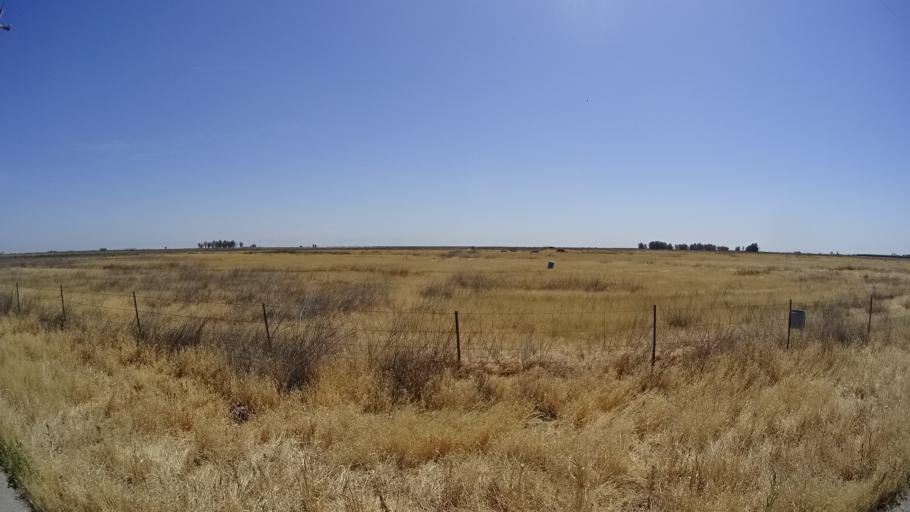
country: US
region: California
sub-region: Kings County
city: Stratford
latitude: 36.1764
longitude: -119.7803
